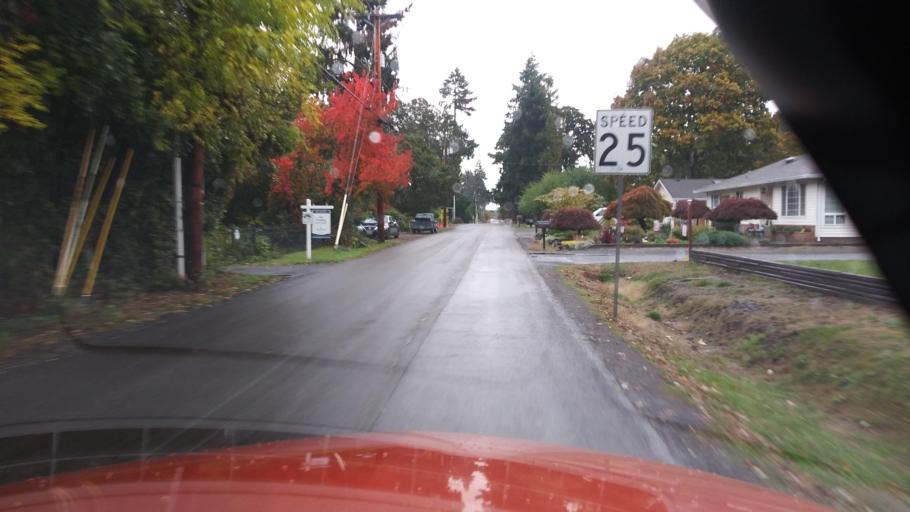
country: US
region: Oregon
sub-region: Washington County
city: Forest Grove
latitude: 45.5274
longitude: -123.1076
